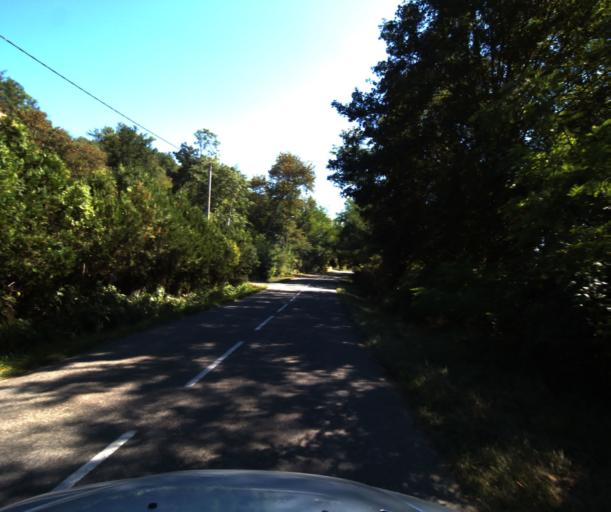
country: FR
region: Midi-Pyrenees
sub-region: Departement de la Haute-Garonne
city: Eaunes
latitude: 43.4341
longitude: 1.3261
